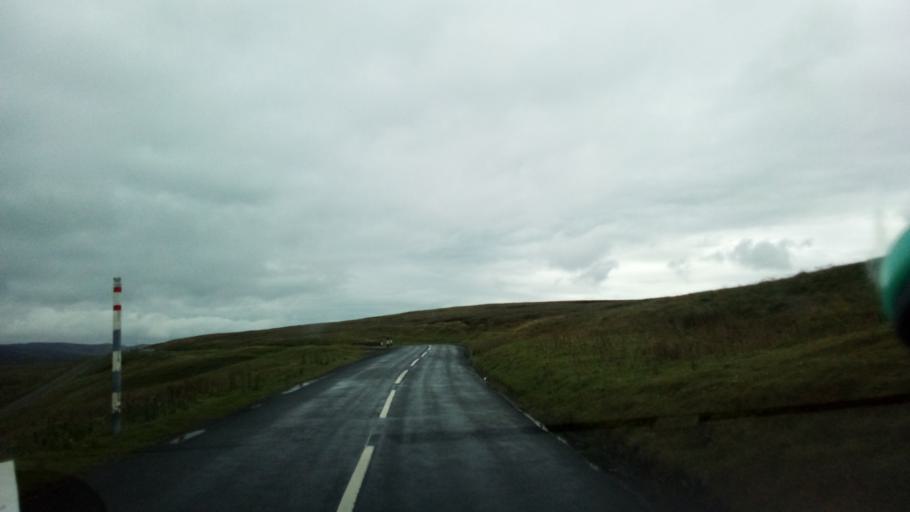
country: GB
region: England
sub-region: County Durham
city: Holwick
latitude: 54.5777
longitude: -2.2410
